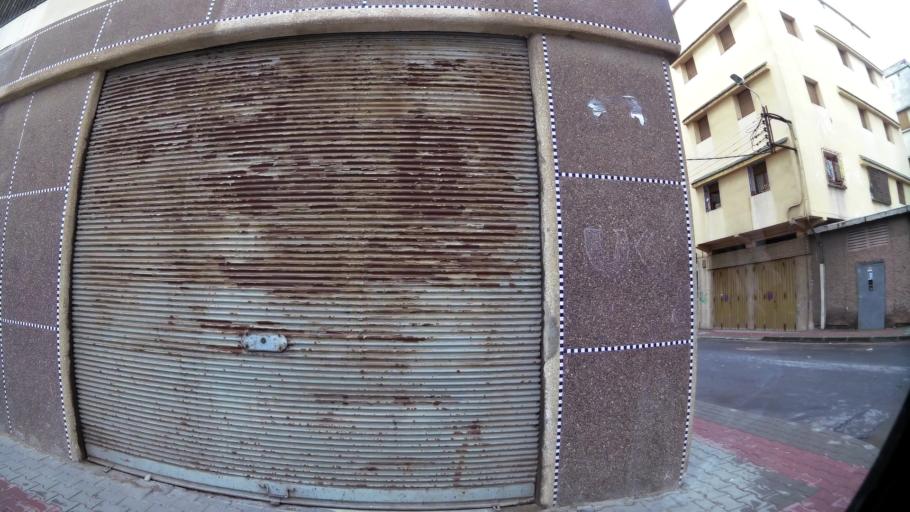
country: MA
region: Grand Casablanca
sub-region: Casablanca
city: Casablanca
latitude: 33.5375
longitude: -7.5754
